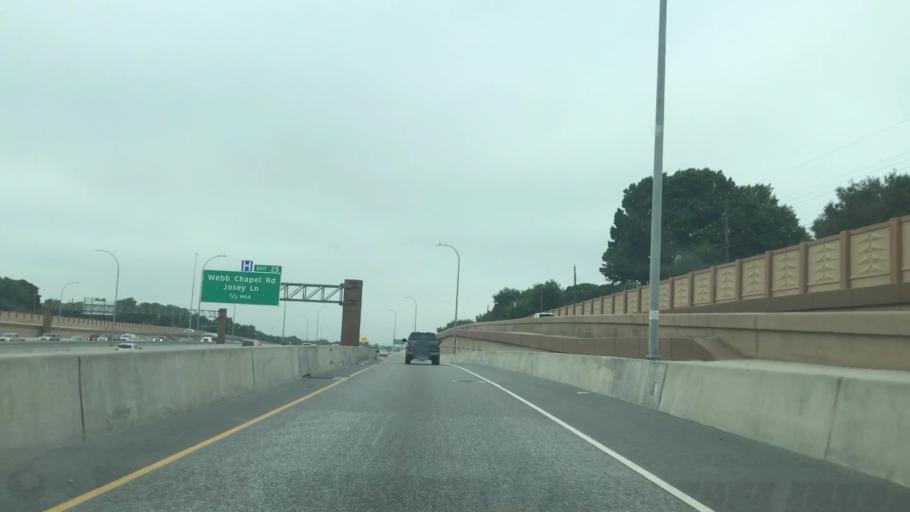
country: US
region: Texas
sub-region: Dallas County
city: Addison
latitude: 32.9214
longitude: -96.8490
